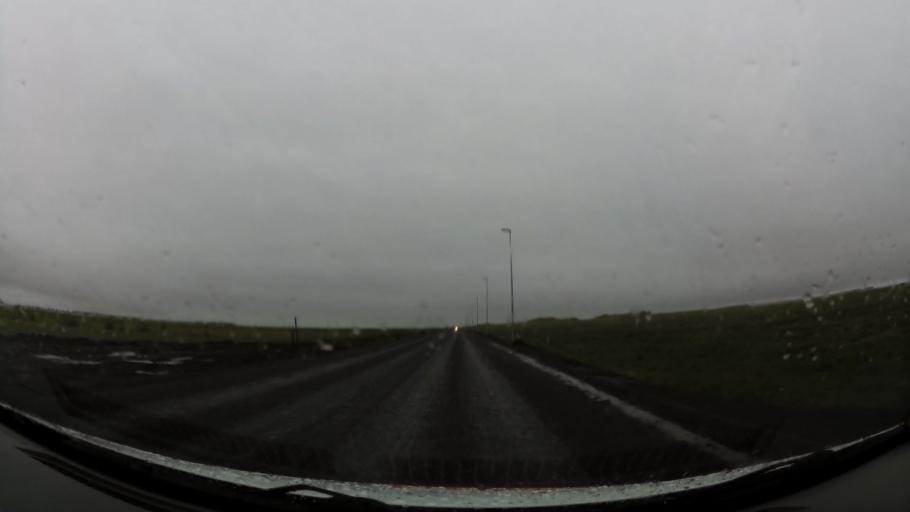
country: IS
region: South
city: Selfoss
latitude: 63.9269
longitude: -20.9735
